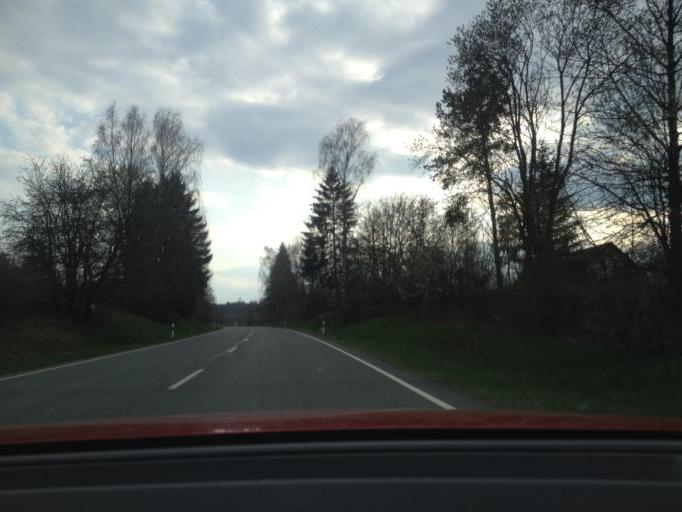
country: DE
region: Bavaria
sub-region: Upper Palatinate
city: Kirchenthumbach
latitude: 49.7448
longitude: 11.7286
